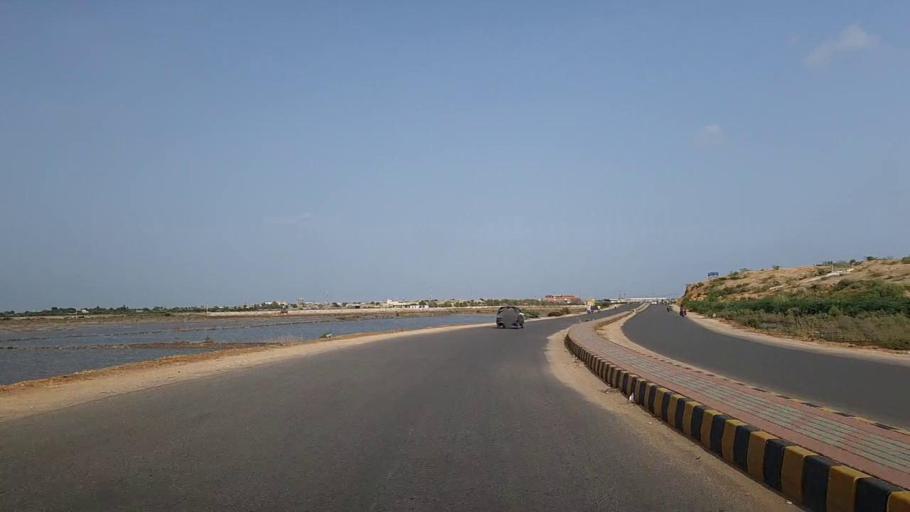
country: PK
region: Sindh
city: Thatta
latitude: 24.7521
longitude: 67.9019
